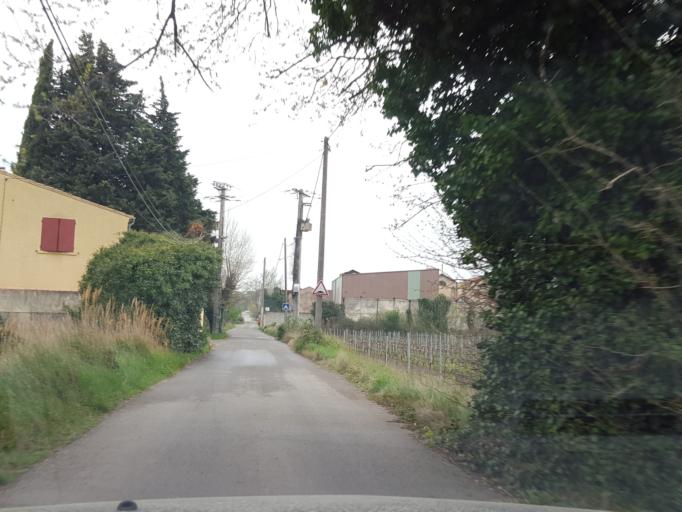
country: FR
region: Provence-Alpes-Cote d'Azur
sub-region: Departement du Vaucluse
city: Saint-Saturnin-les-Avignon
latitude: 43.9685
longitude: 4.9317
